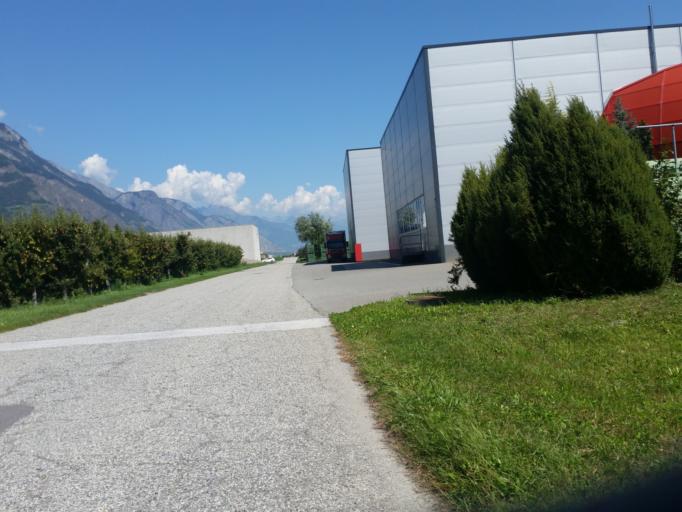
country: CH
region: Valais
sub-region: Martigny District
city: Charrat-les-Chenes
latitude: 46.1270
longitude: 7.1223
